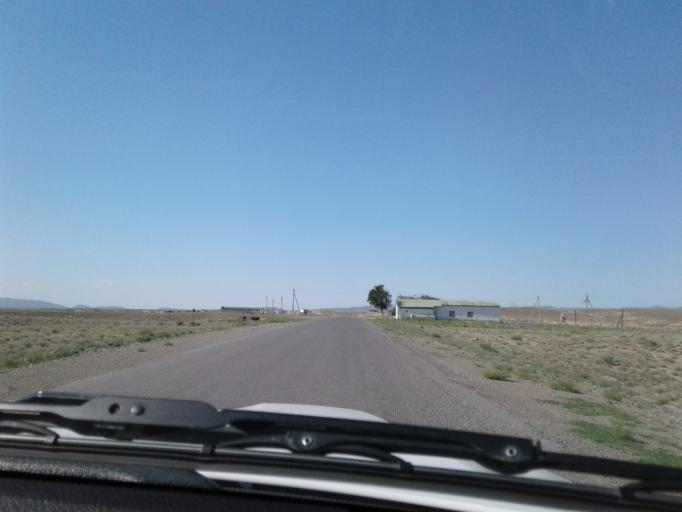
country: TM
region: Balkan
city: Serdar
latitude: 38.7200
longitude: 56.2930
